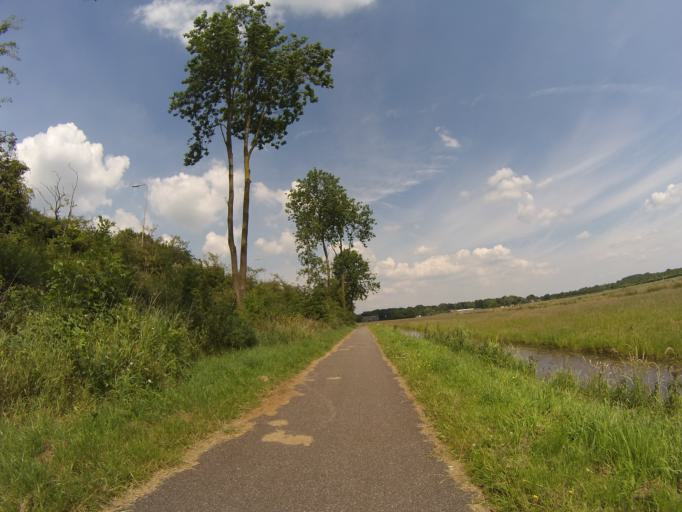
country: NL
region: Utrecht
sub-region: Gemeente De Bilt
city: De Bilt
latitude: 52.1163
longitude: 5.1488
